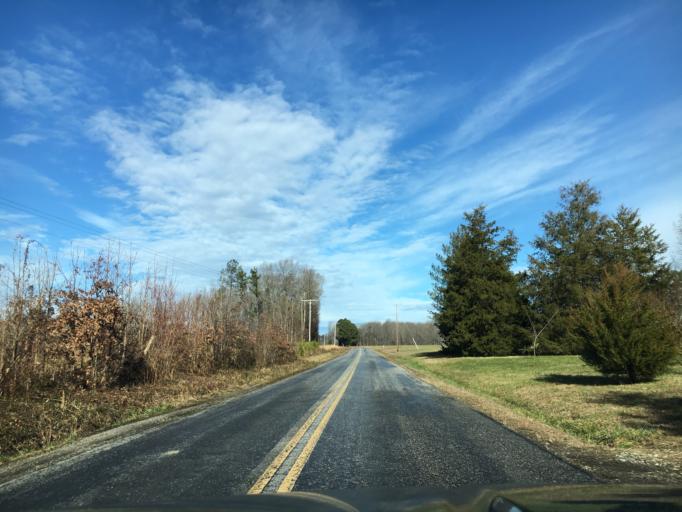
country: US
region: Virginia
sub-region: Cumberland County
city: Cumberland
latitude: 37.3616
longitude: -78.1558
